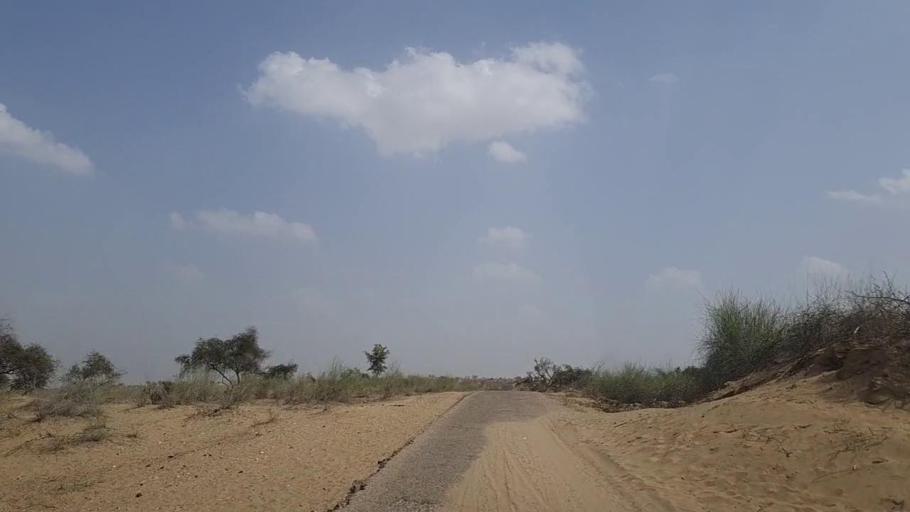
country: PK
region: Sindh
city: Islamkot
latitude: 24.7872
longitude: 70.0900
